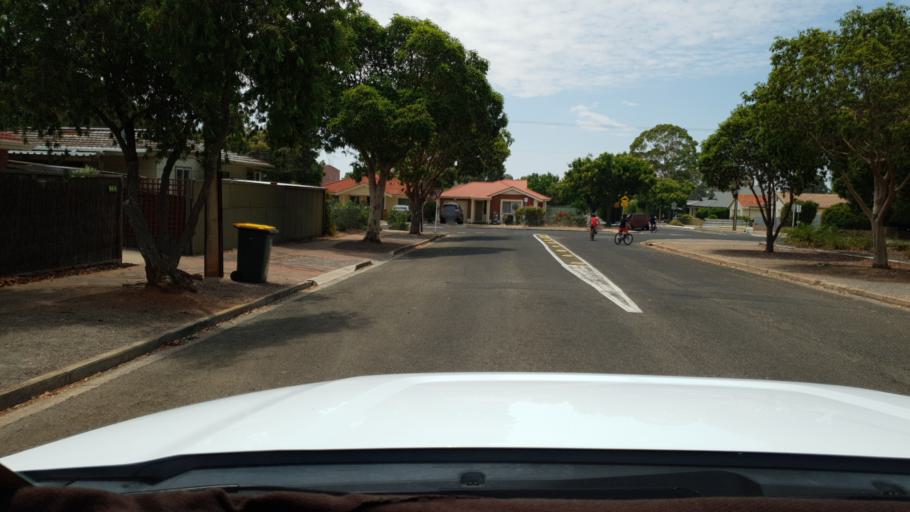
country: AU
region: South Australia
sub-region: Marion
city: Clovelly Park
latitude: -35.0011
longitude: 138.5790
